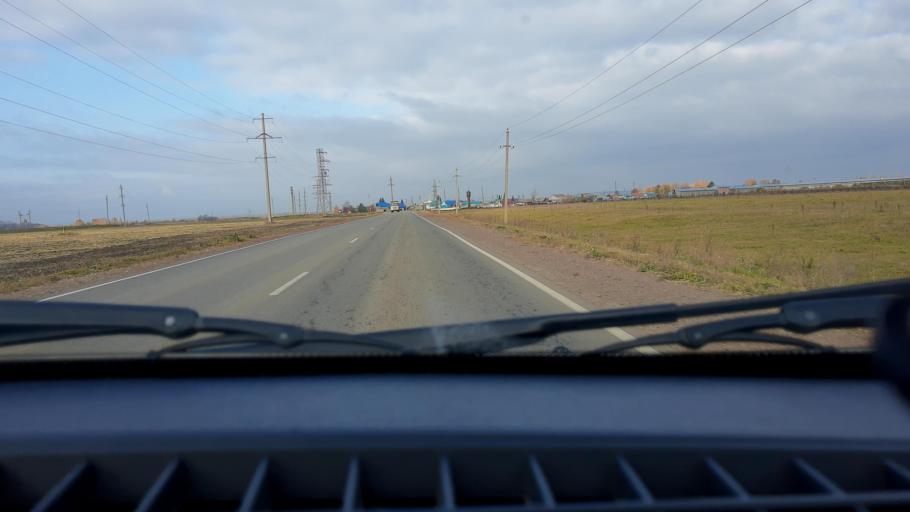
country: RU
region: Bashkortostan
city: Kabakovo
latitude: 54.5446
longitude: 56.0457
